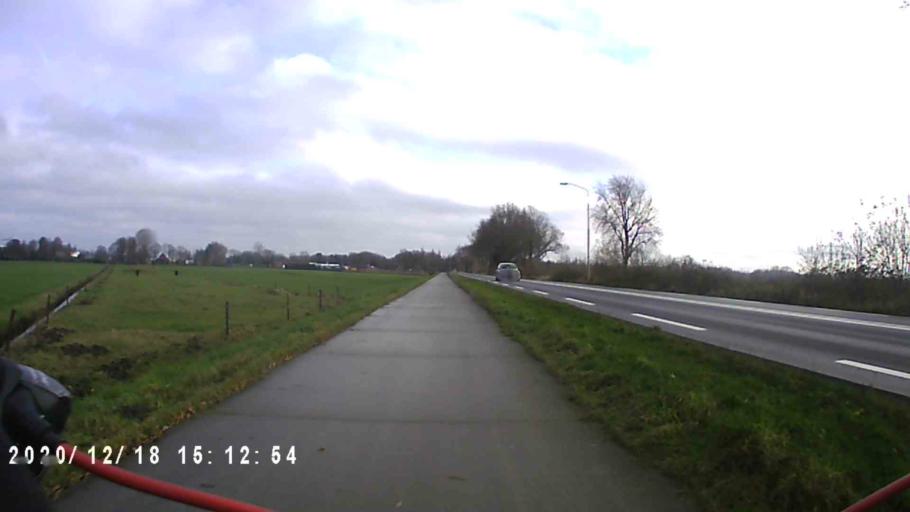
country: NL
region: Groningen
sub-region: Gemeente Hoogezand-Sappemeer
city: Hoogezand
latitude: 53.1641
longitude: 6.7149
